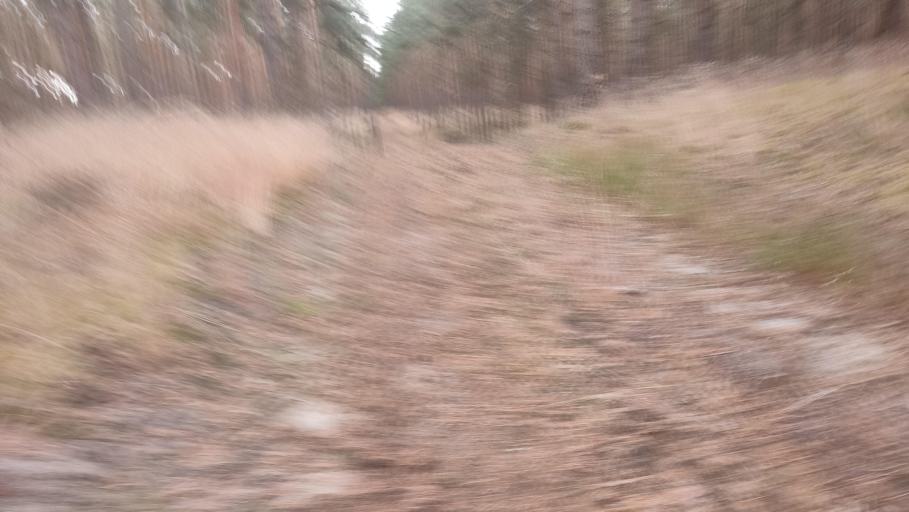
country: DE
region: Lower Saxony
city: Hitzacker
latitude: 53.2070
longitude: 11.0735
